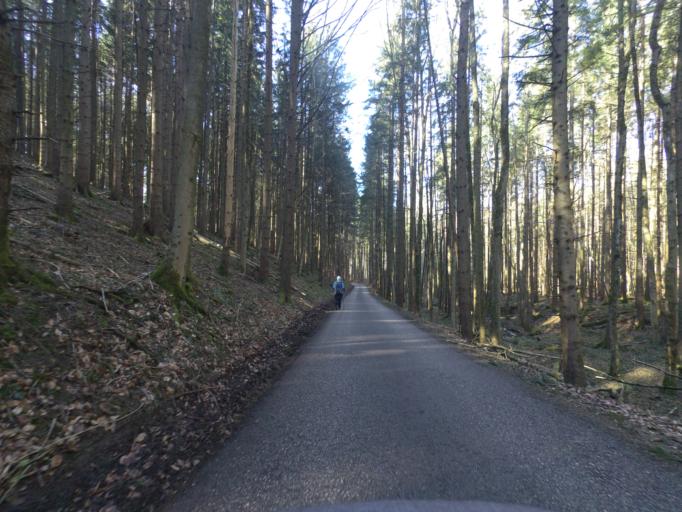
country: DE
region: Bavaria
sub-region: Upper Bavaria
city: Piding
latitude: 47.7857
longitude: 12.9144
